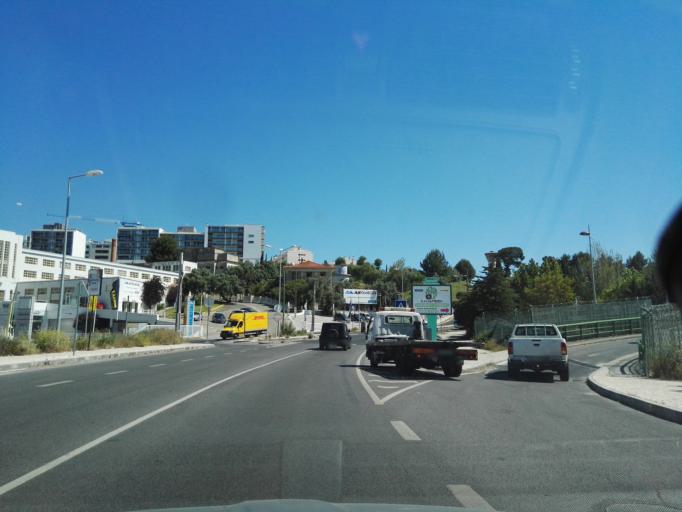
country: PT
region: Lisbon
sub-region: Loures
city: Sacavem
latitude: 38.7981
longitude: -9.1044
